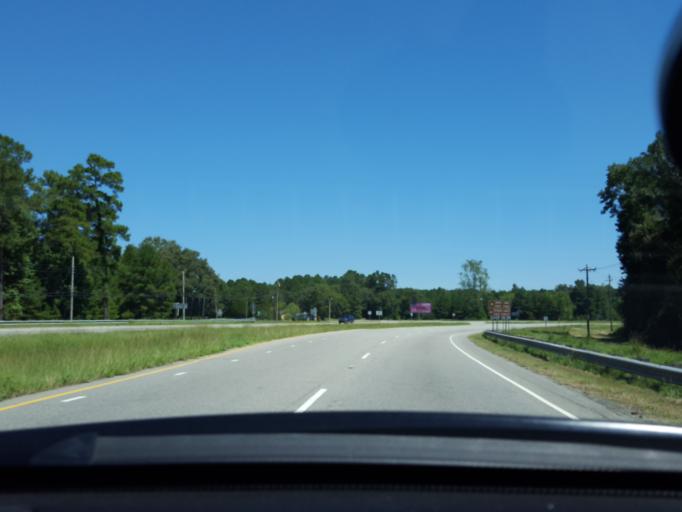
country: US
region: North Carolina
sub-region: Bladen County
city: Elizabethtown
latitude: 34.6433
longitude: -78.5941
